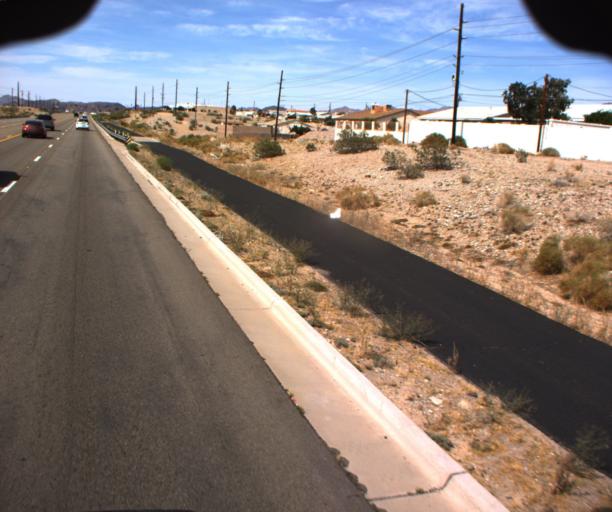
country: US
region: Arizona
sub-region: Mohave County
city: Lake Havasu City
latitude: 34.5124
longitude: -114.3494
